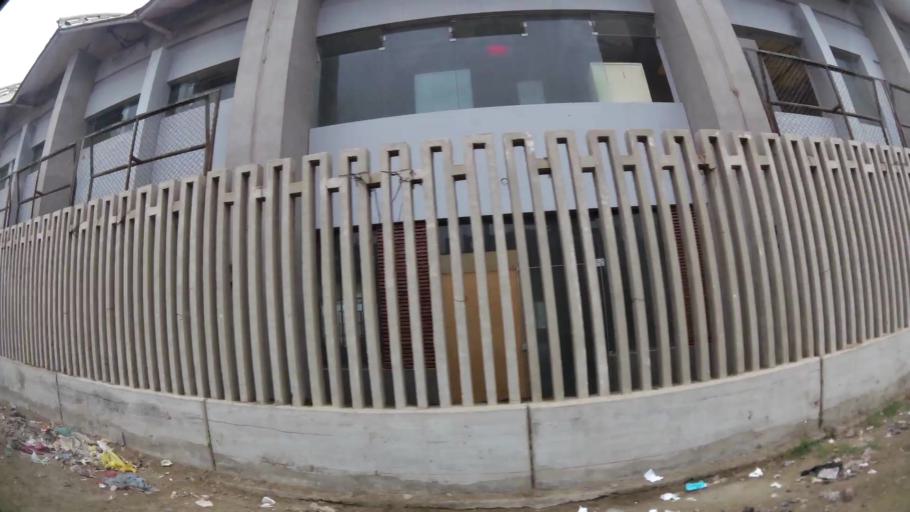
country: PE
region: Ica
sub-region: Provincia de Pisco
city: Pisco
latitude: -13.7179
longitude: -76.2158
